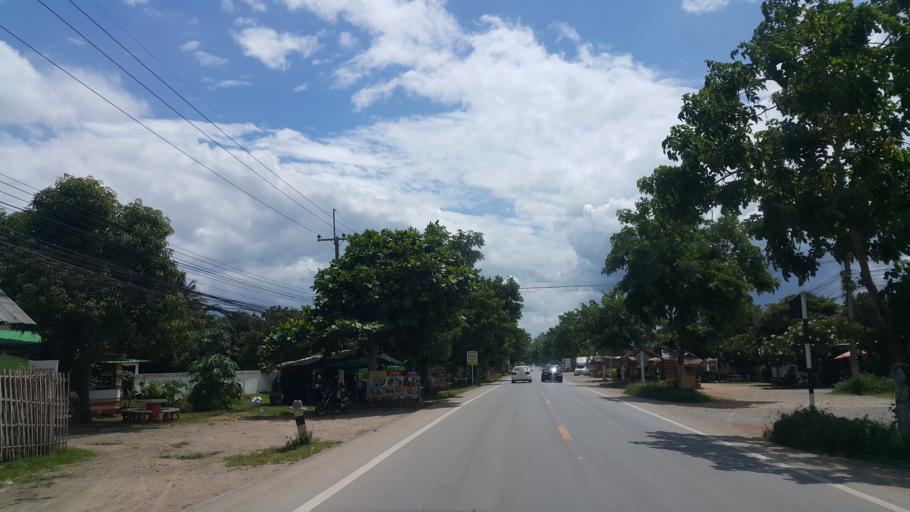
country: TH
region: Chiang Mai
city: Mae Taeng
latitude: 19.1448
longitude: 99.0017
